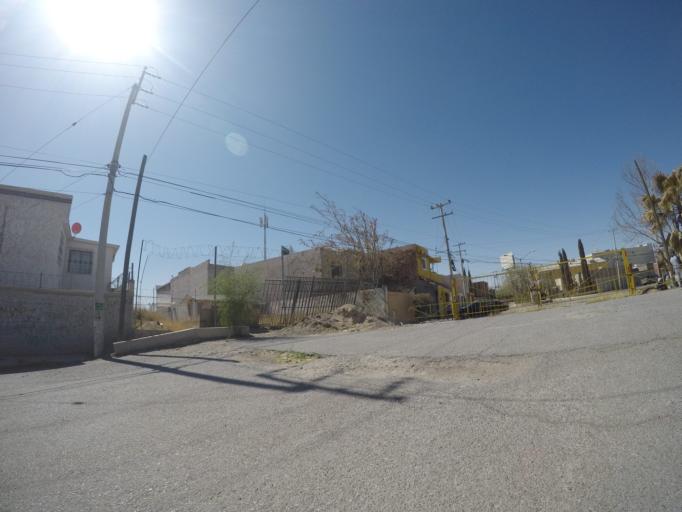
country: MX
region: Chihuahua
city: Ciudad Juarez
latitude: 31.6894
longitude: -106.4169
